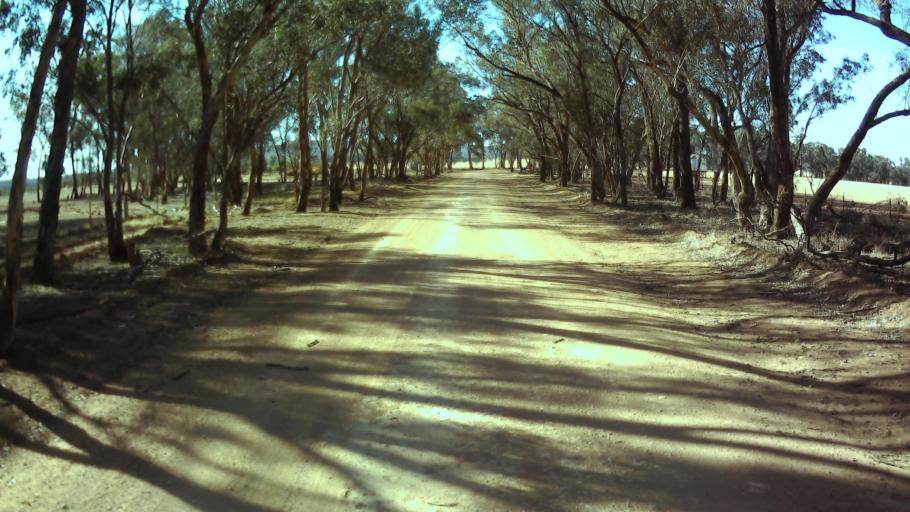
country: AU
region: New South Wales
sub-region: Weddin
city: Grenfell
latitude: -33.8370
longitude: 147.8738
